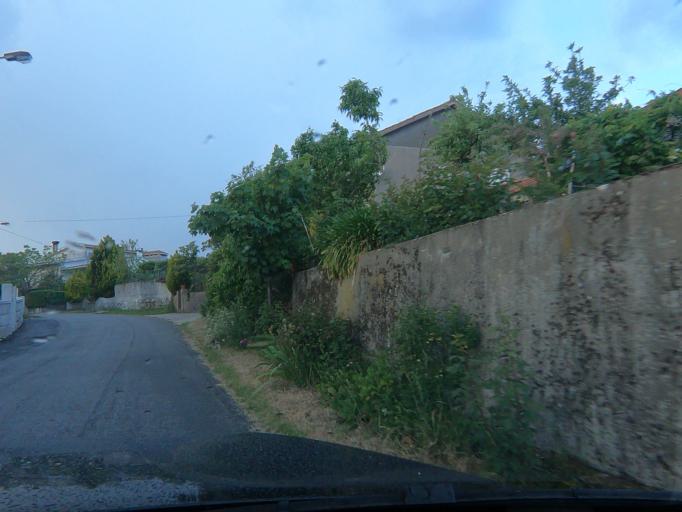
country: PT
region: Vila Real
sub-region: Vila Real
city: Vila Real
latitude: 41.3170
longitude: -7.6832
